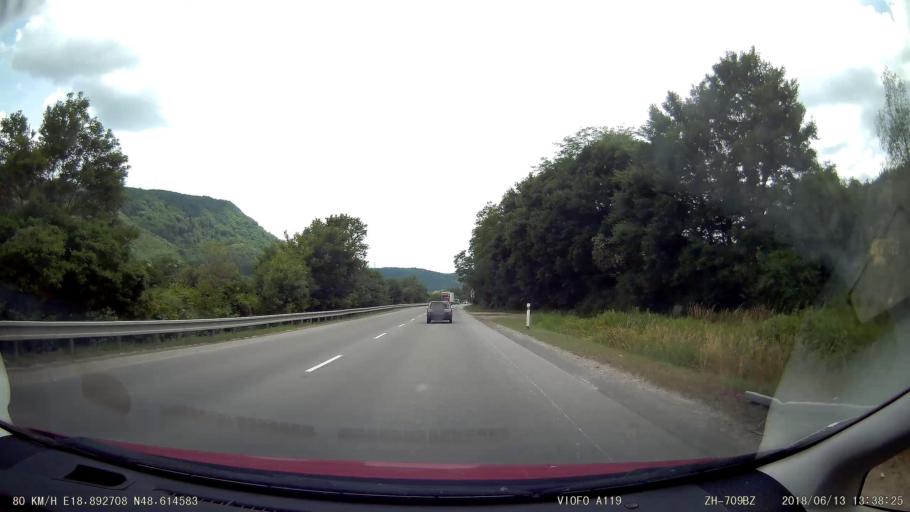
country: SK
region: Banskobystricky
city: Ziar nad Hronom
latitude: 48.6144
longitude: 18.8927
